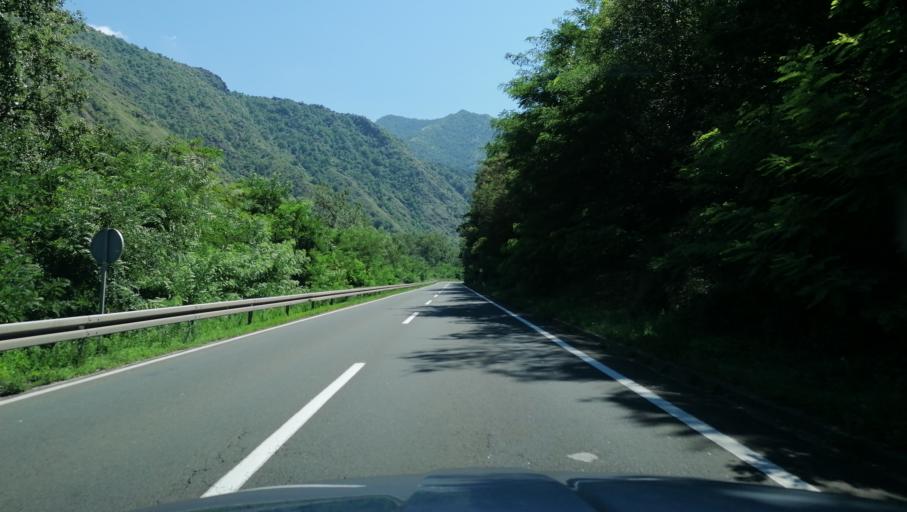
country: RS
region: Central Serbia
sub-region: Raski Okrug
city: Kraljevo
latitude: 43.6232
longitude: 20.5484
